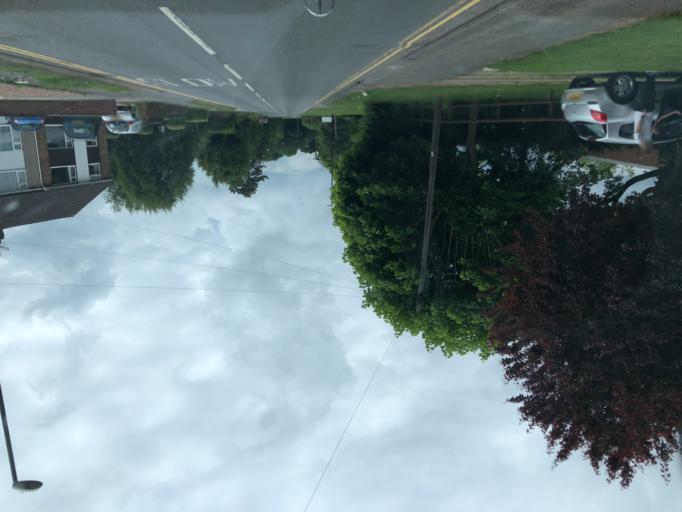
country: GB
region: England
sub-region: Warwickshire
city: Kenilworth
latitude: 52.3929
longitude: -1.5960
